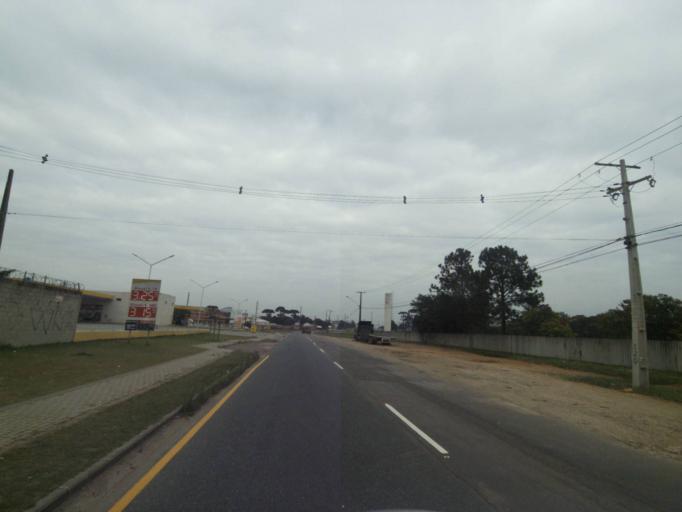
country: BR
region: Parana
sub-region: Curitiba
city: Curitiba
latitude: -25.5186
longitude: -49.3276
